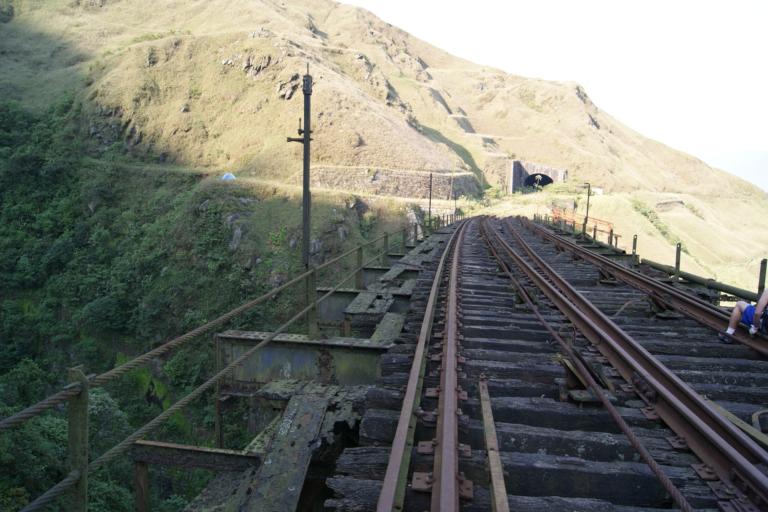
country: BR
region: Sao Paulo
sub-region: Rio Grande Da Serra
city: Rio Grande da Serra
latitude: -23.7930
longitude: -46.3158
